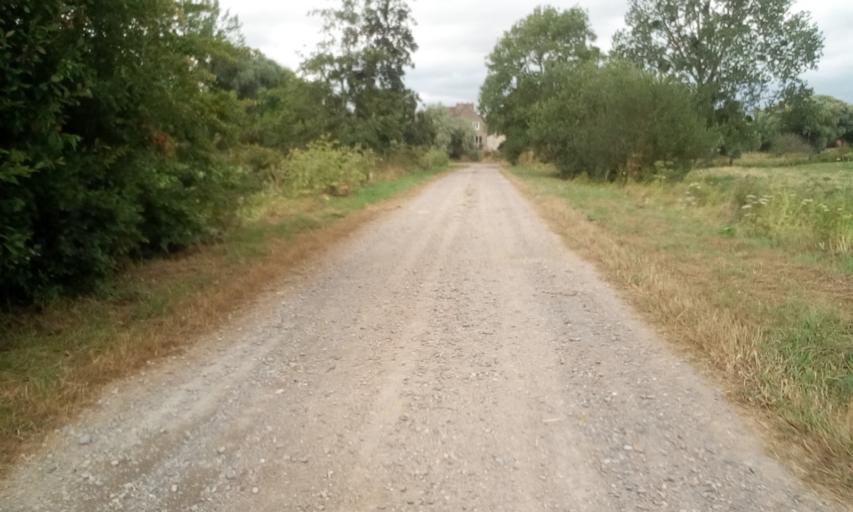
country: FR
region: Lower Normandy
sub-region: Departement du Calvados
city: Troarn
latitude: 49.1965
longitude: -0.1716
